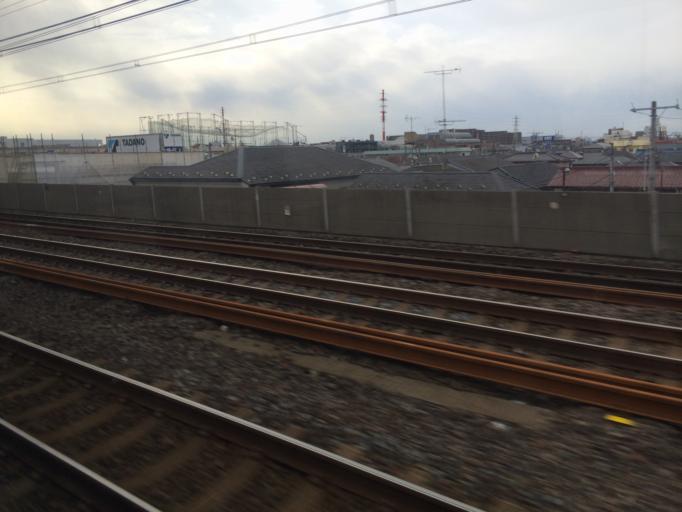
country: JP
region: Chiba
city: Funabashi
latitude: 35.7192
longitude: 139.9315
